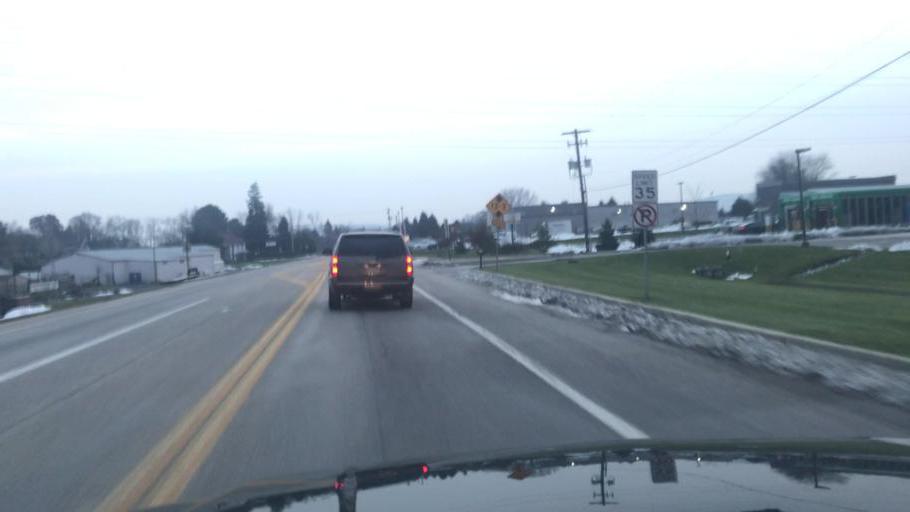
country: US
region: Pennsylvania
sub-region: Cumberland County
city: Mechanicsburg
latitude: 40.1761
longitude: -76.9847
